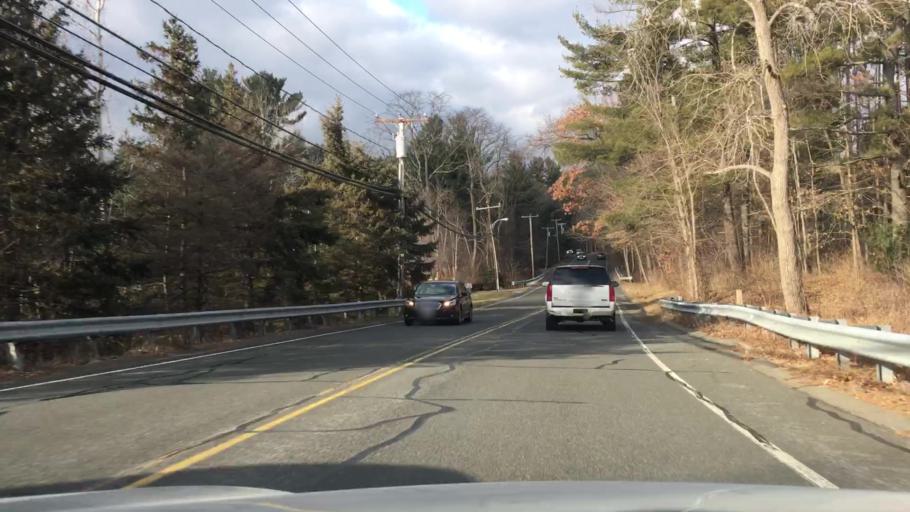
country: US
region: Massachusetts
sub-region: Hampden County
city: Longmeadow
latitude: 42.0429
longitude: -72.5718
